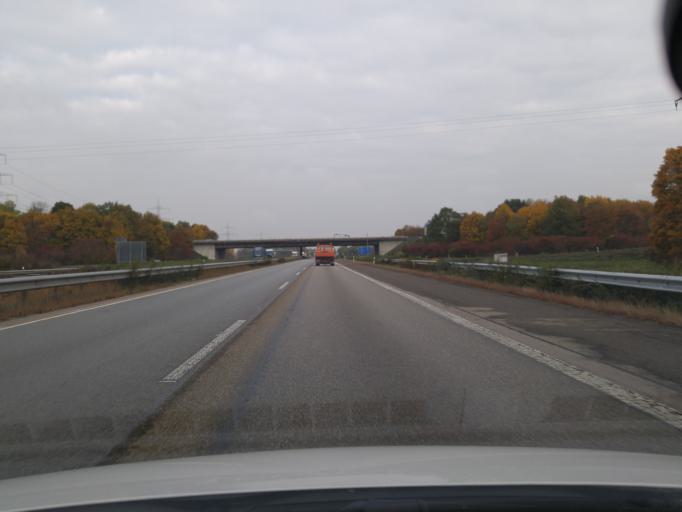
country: DE
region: Rheinland-Pfalz
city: Dannstadt-Schauernheim
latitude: 49.4410
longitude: 8.3255
